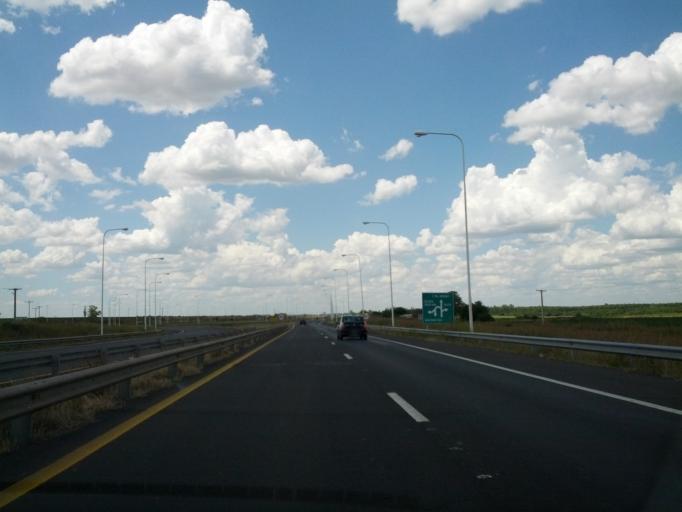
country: AR
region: Entre Rios
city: Colonia Elia
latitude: -32.5436
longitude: -58.3491
